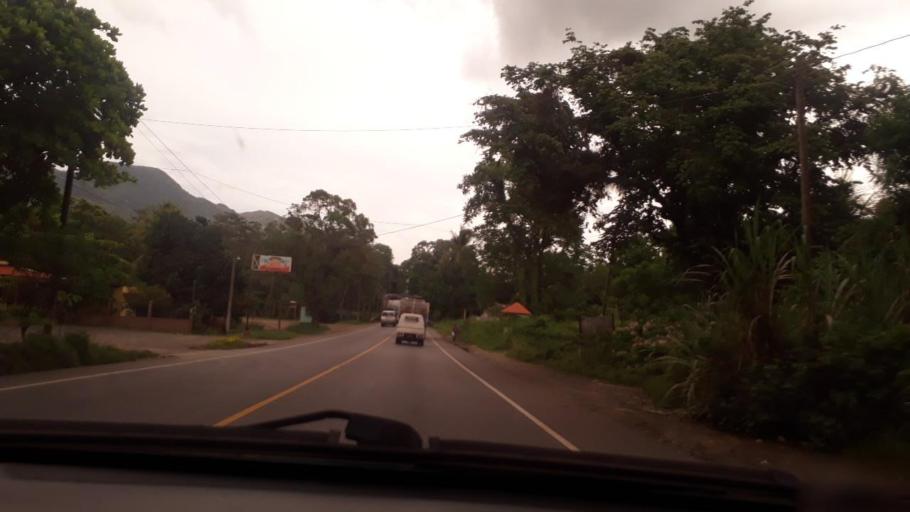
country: GT
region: Izabal
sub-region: Municipio de Los Amates
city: Los Amates
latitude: 15.2354
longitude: -89.1856
